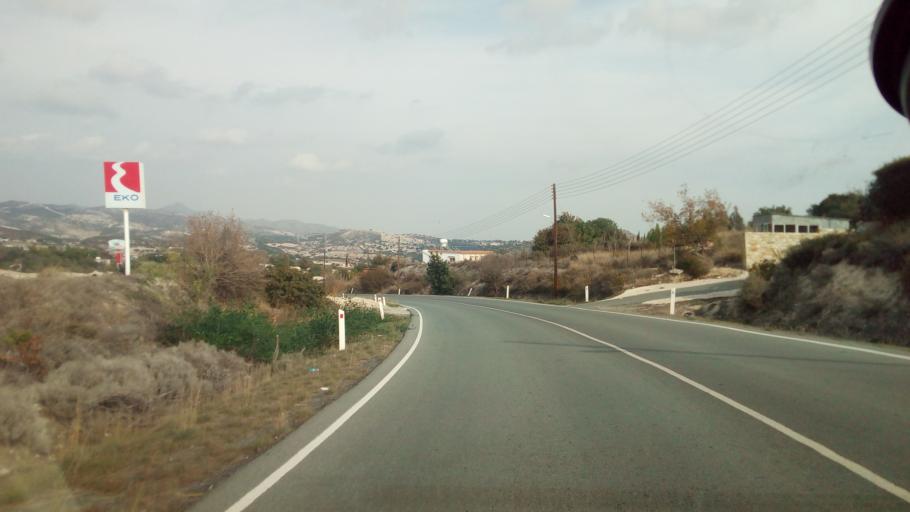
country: CY
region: Larnaka
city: Kofinou
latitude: 34.8142
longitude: 33.3602
